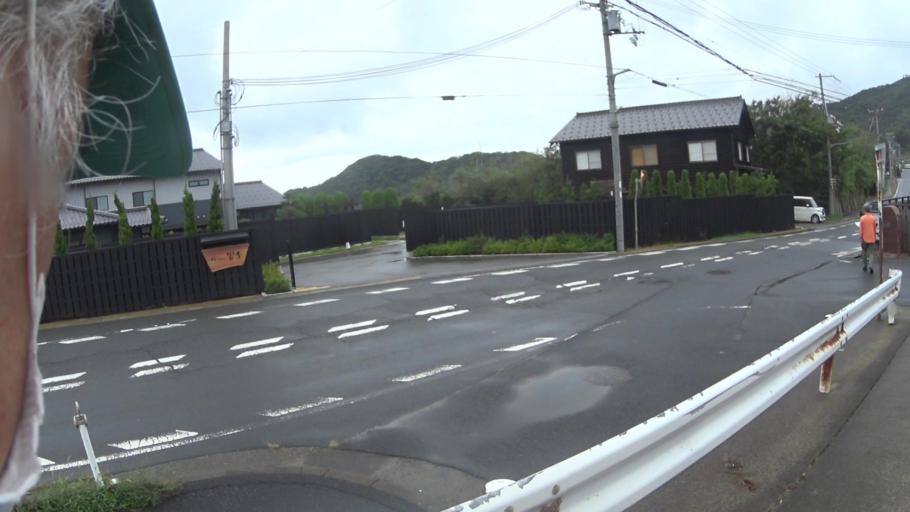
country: JP
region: Hyogo
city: Toyooka
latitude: 35.6614
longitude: 134.9637
